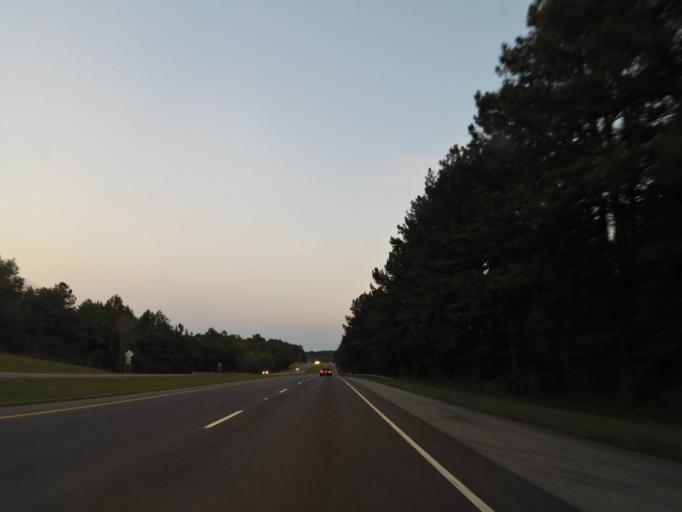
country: US
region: Tennessee
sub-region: Knox County
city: Farragut
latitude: 35.9594
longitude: -84.1680
